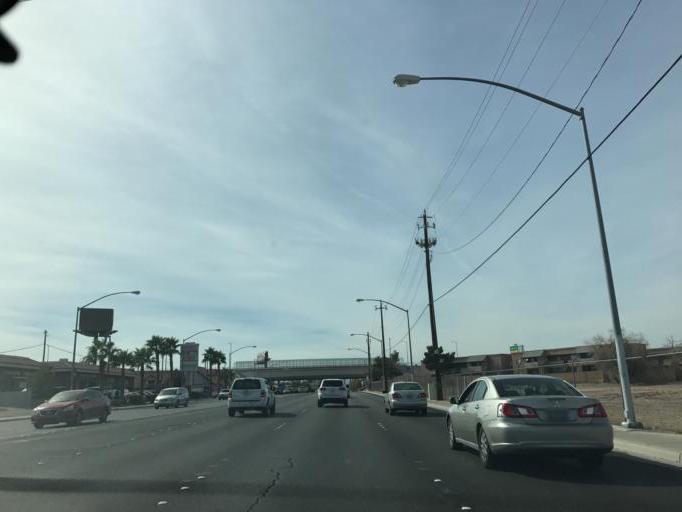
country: US
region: Nevada
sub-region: Clark County
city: Winchester
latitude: 36.1296
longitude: -115.0863
